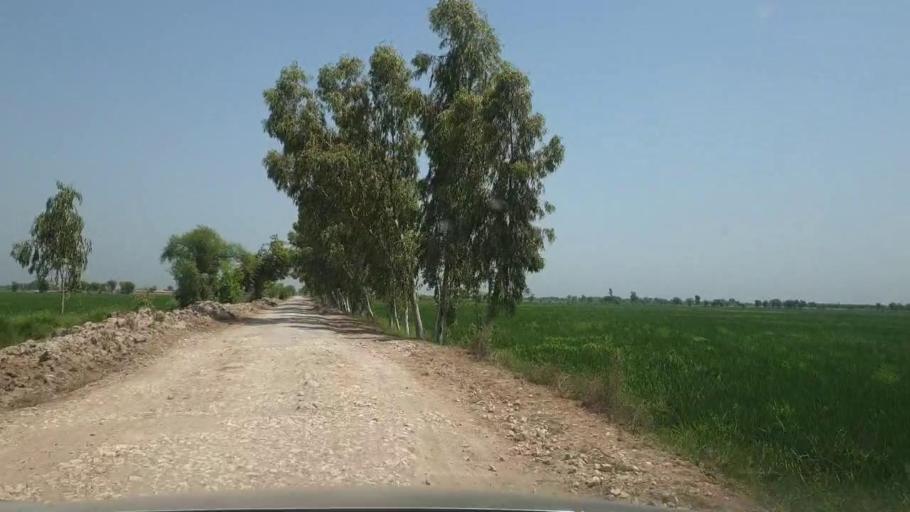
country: PK
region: Sindh
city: Warah
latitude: 27.5092
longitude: 67.7731
